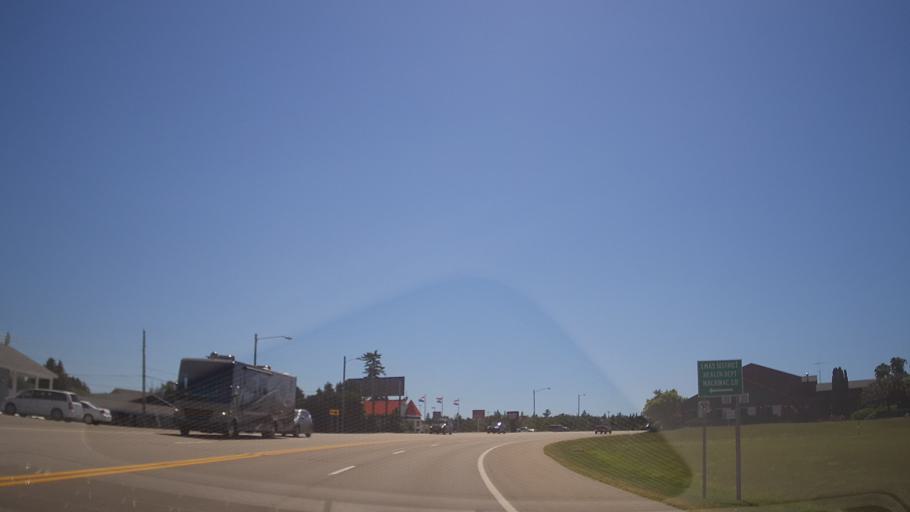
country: US
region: Michigan
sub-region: Mackinac County
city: Saint Ignace
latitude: 45.8596
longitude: -84.7168
